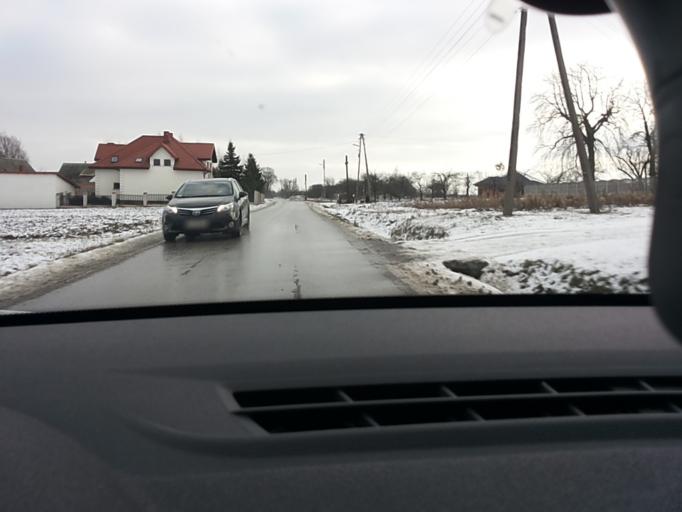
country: PL
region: Lodz Voivodeship
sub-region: Powiat skierniewicki
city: Makow
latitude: 51.9883
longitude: 20.0898
